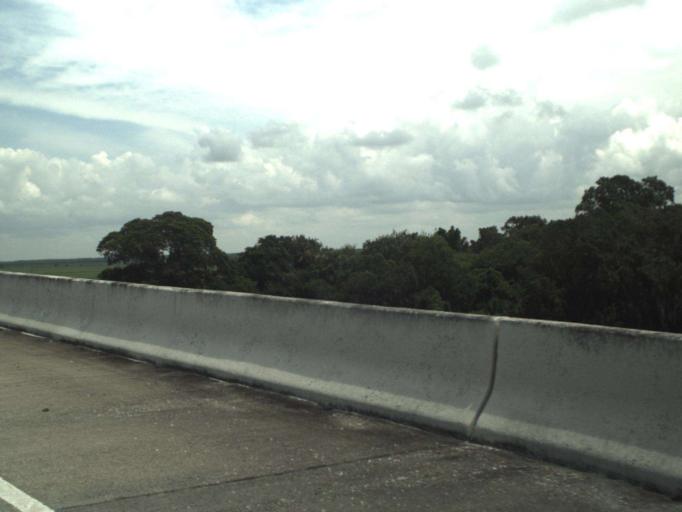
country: US
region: Florida
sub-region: Martin County
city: Indiantown
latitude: 26.9830
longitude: -80.6163
